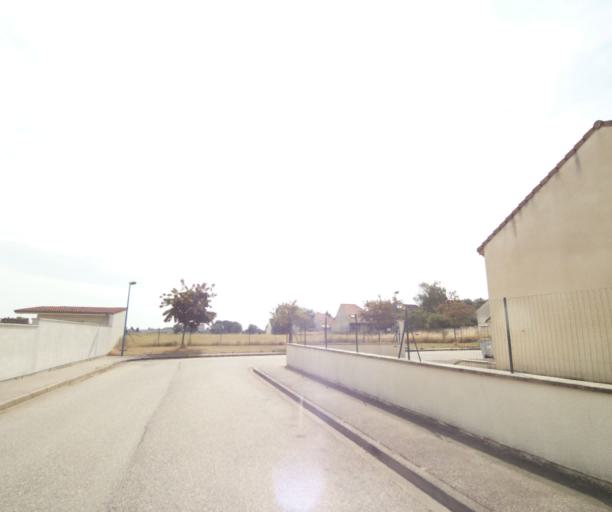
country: FR
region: Lorraine
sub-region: Departement de Meurthe-et-Moselle
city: Luneville
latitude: 48.5937
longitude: 6.5122
